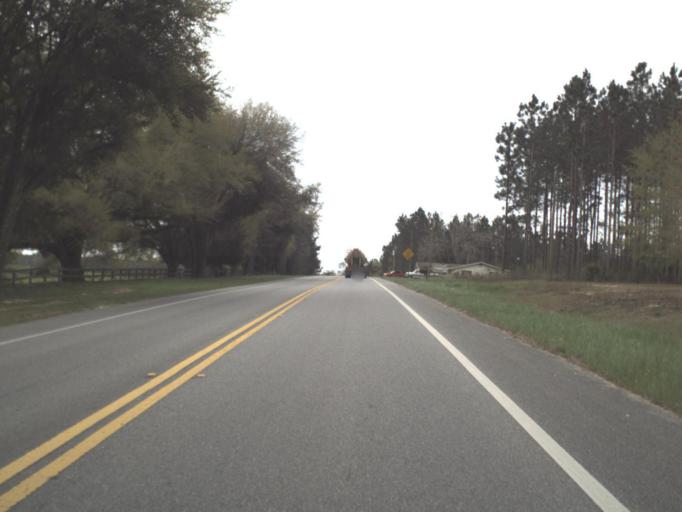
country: US
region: Florida
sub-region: Holmes County
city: Bonifay
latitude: 30.8698
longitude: -85.6650
